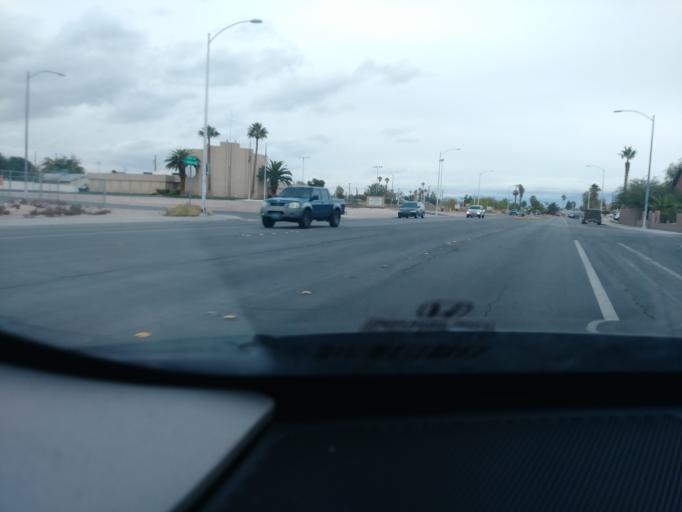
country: US
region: Nevada
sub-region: Clark County
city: Spring Valley
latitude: 36.1607
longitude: -115.2193
